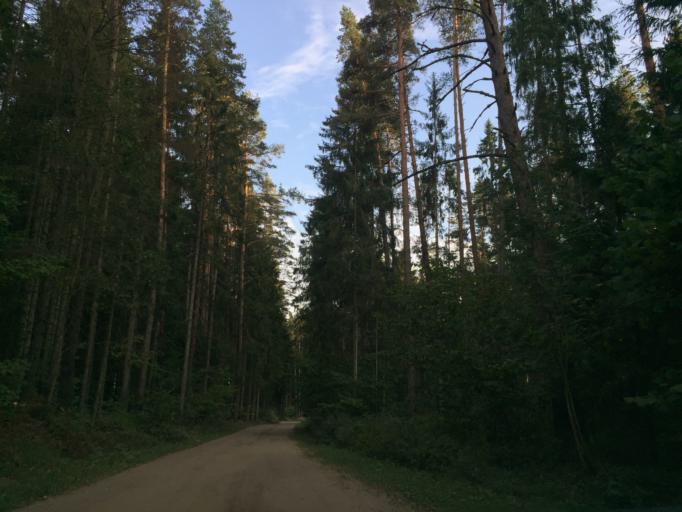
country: LV
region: Baldone
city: Baldone
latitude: 56.7684
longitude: 24.4044
